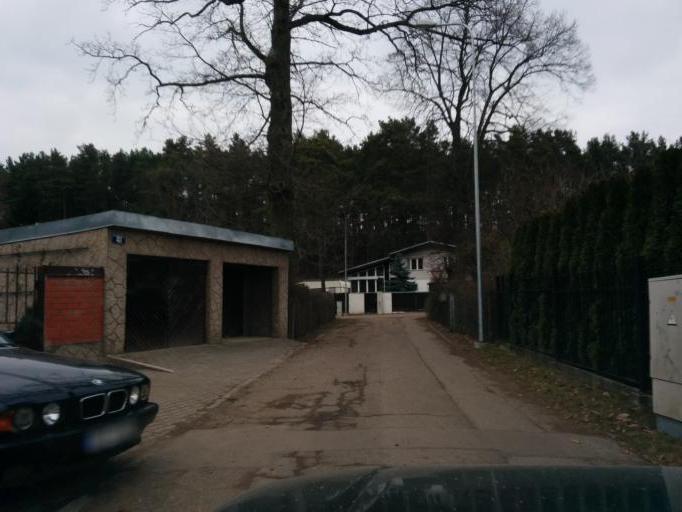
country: LV
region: Babite
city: Pinki
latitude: 56.9951
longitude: 23.9180
